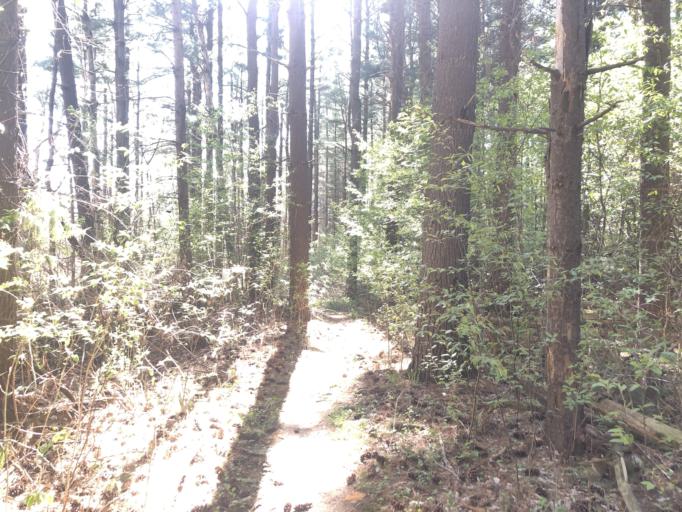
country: US
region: Michigan
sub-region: Eaton County
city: Waverly
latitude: 42.6947
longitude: -84.6241
